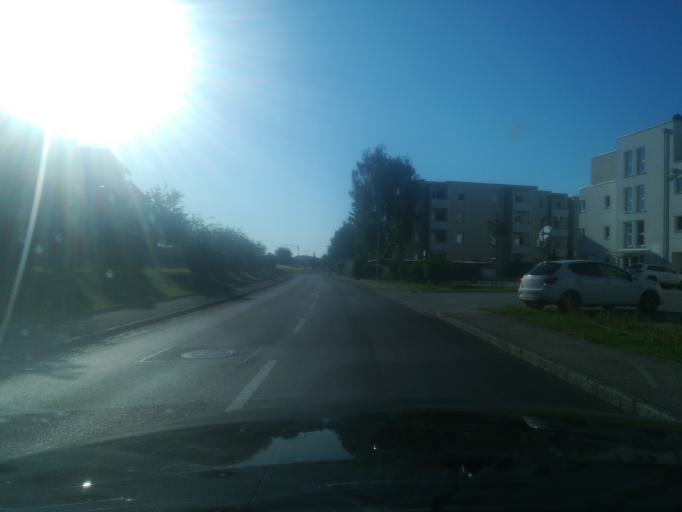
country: AT
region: Upper Austria
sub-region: Politischer Bezirk Urfahr-Umgebung
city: Gallneukirchen
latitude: 48.3481
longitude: 14.4229
